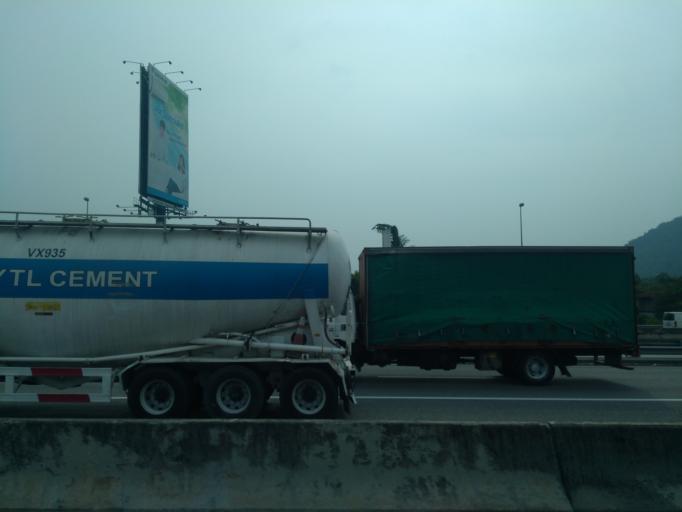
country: MY
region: Perak
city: Ipoh
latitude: 4.5894
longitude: 101.1445
